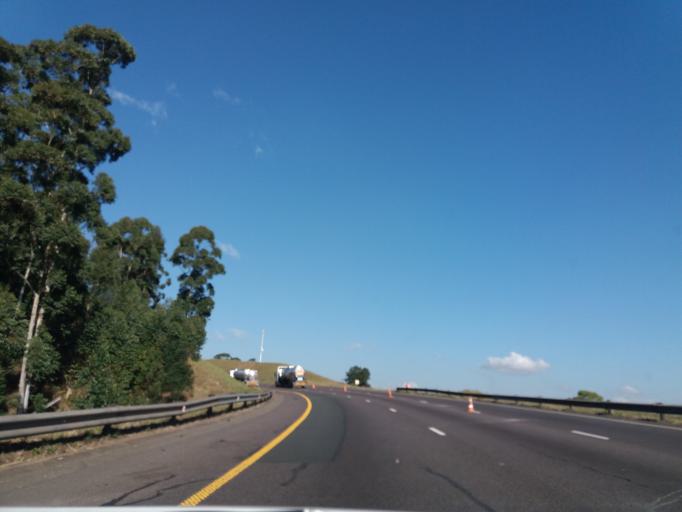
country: ZA
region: KwaZulu-Natal
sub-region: eThekwini Metropolitan Municipality
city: Mpumalanga
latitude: -29.7818
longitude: 30.7113
